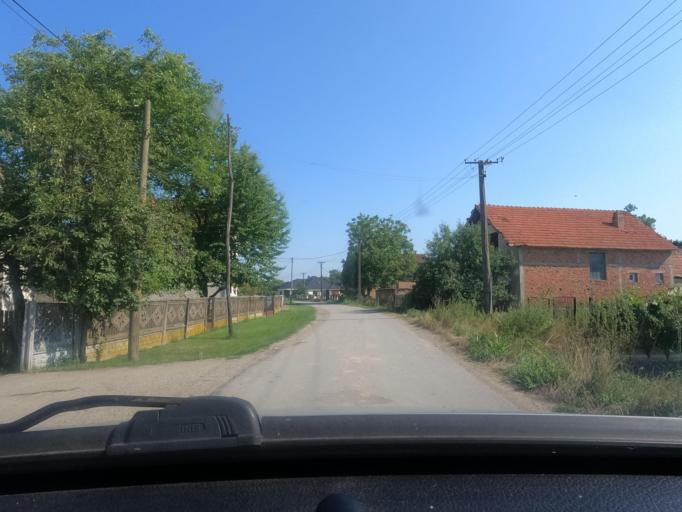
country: RS
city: Bogosavac
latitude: 44.7497
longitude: 19.5819
